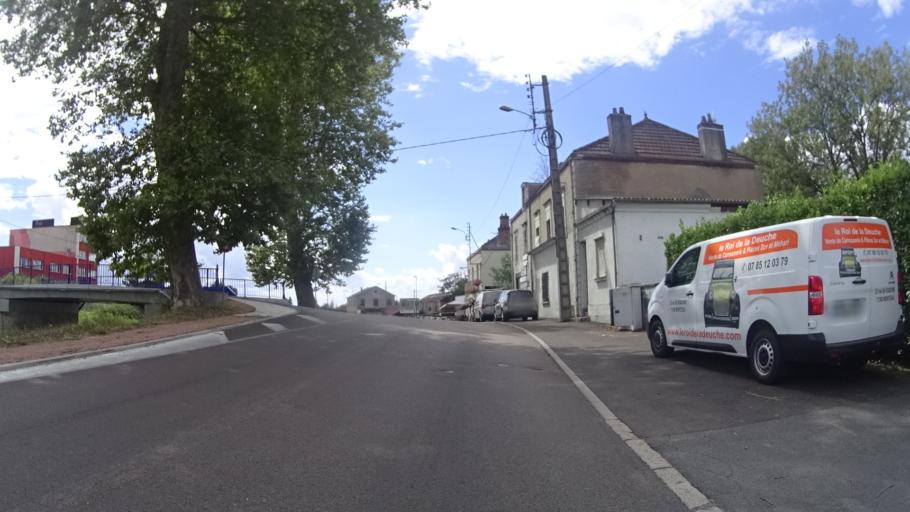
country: FR
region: Bourgogne
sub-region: Departement de Saone-et-Loire
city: Montceau-les-Mines
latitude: 46.6625
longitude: 4.3488
